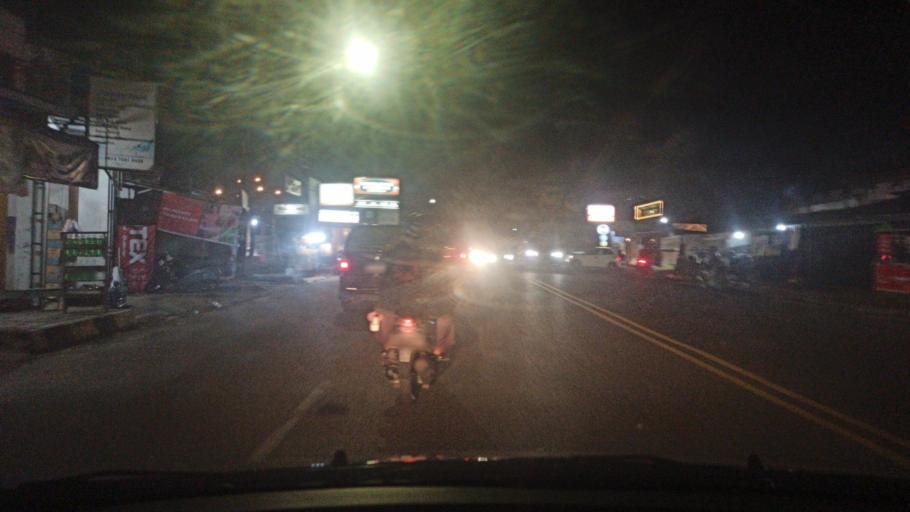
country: ID
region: South Sumatra
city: Plaju
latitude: -2.9917
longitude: 104.7265
